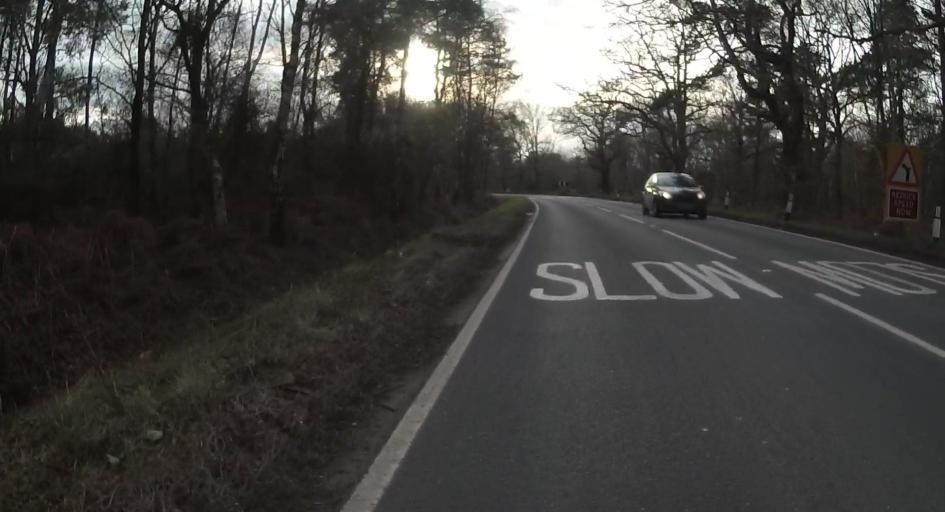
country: GB
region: England
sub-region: Hampshire
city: Tadley
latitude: 51.3787
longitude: -1.1099
